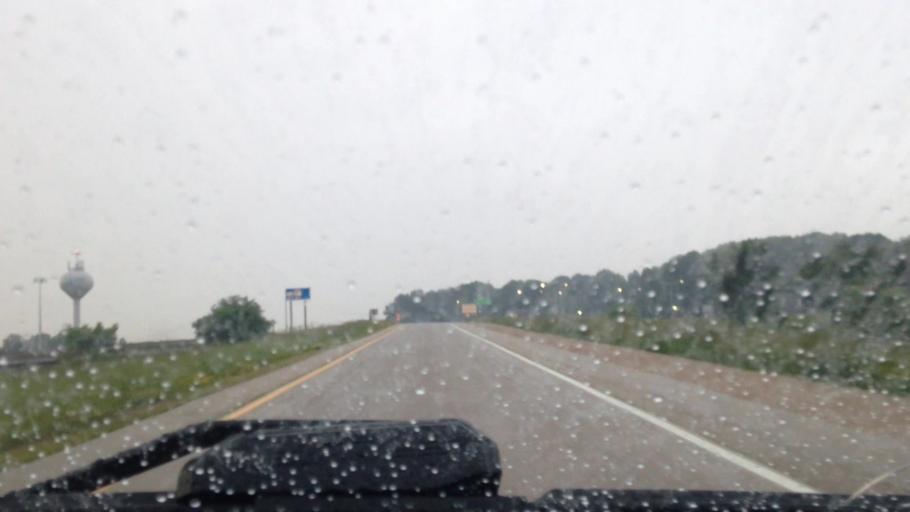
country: US
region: Wisconsin
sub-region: Washington County
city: Slinger
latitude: 43.4224
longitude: -88.3347
